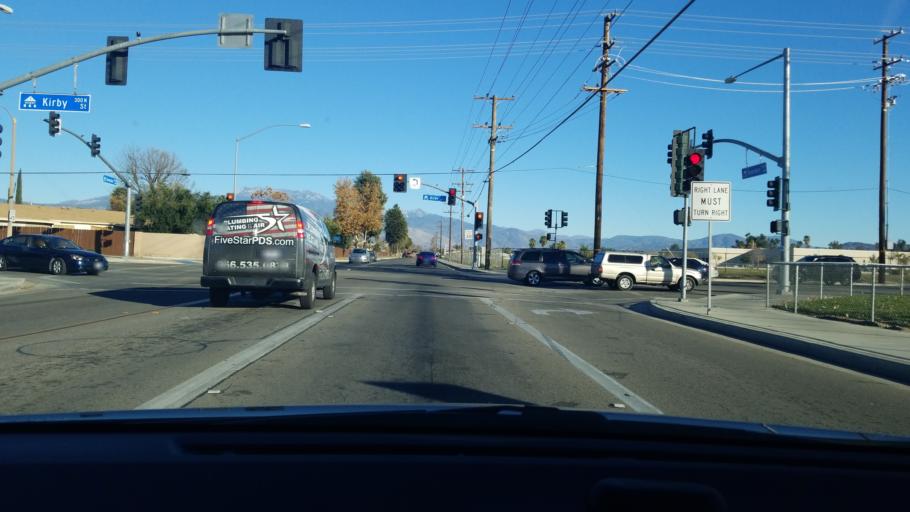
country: US
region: California
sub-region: Riverside County
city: Hemet
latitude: 33.7510
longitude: -116.9982
